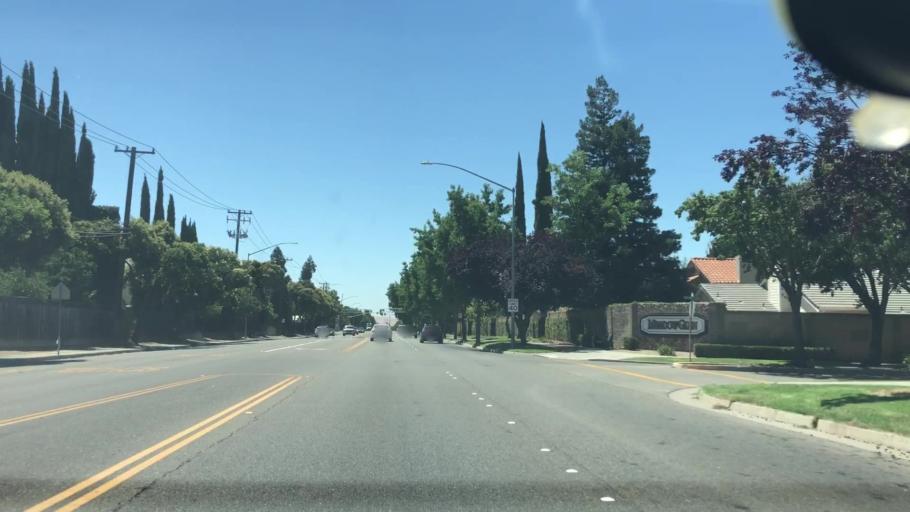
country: US
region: California
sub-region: San Joaquin County
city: Tracy
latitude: 37.7252
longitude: -121.4228
